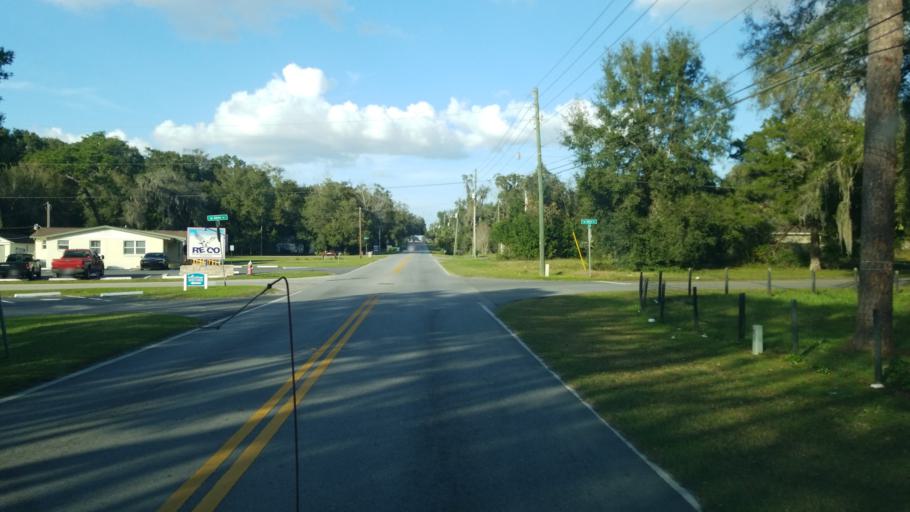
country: US
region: Florida
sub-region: Marion County
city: Ocala
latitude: 29.2067
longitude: -82.1285
